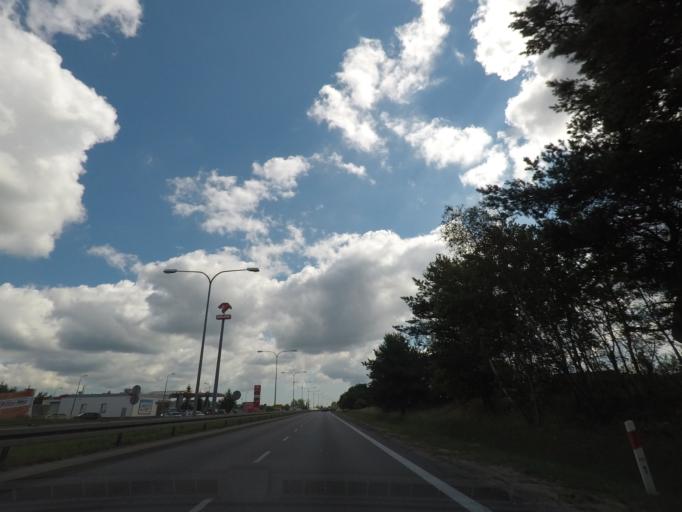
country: PL
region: Pomeranian Voivodeship
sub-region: Powiat wejherowski
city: Bolszewo
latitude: 54.6102
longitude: 18.1881
